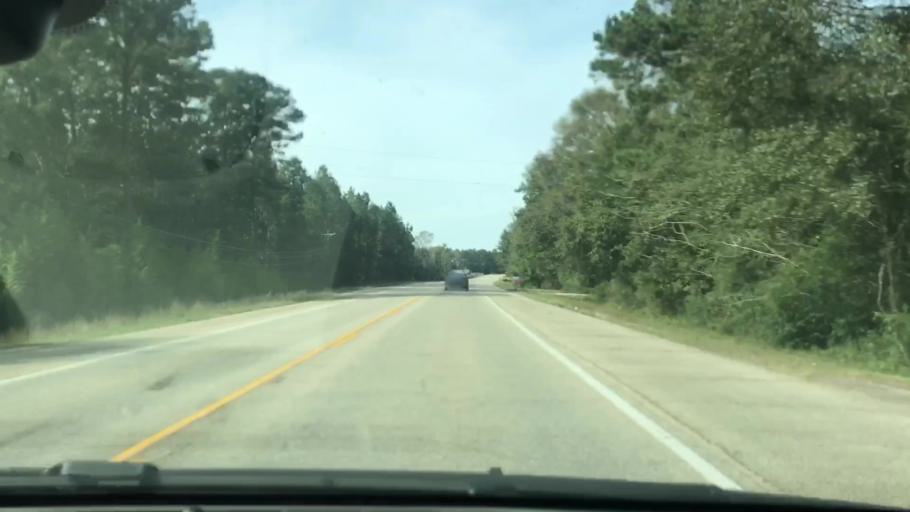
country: US
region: Louisiana
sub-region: Saint Tammany Parish
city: Pearl River
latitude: 30.4620
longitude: -89.8079
